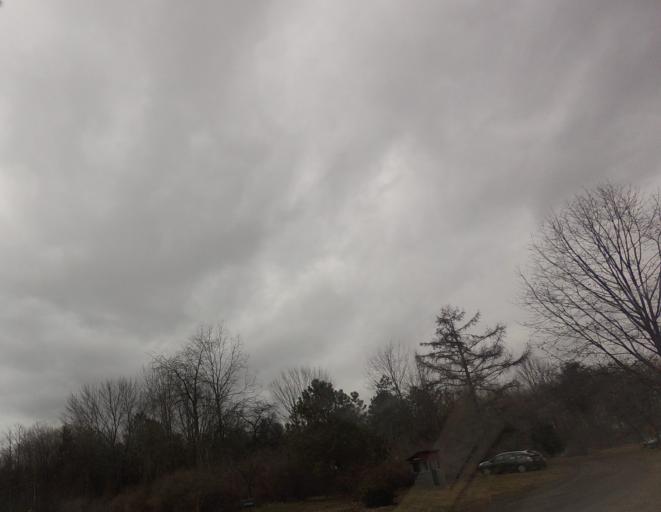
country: US
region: New York
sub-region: Tompkins County
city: Northwest Ithaca
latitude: 42.4371
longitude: -76.5450
